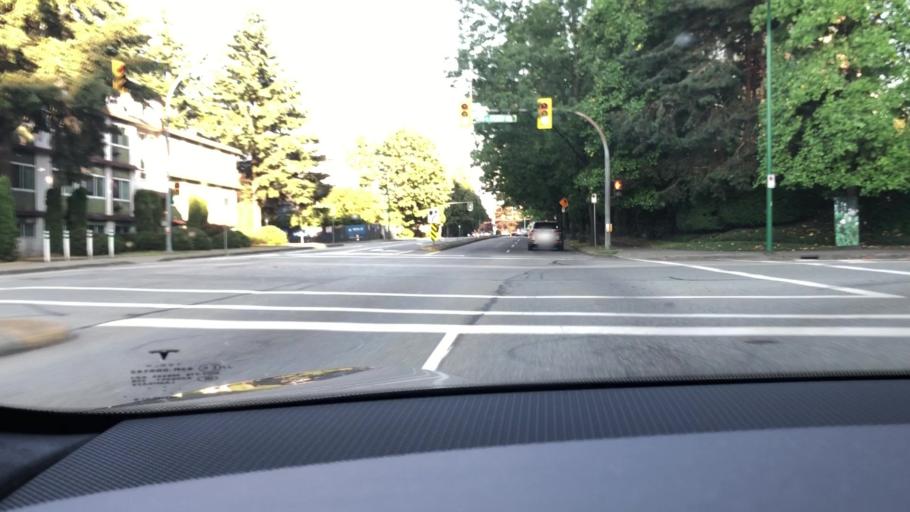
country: CA
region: British Columbia
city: Burnaby
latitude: 49.2309
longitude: -123.0018
